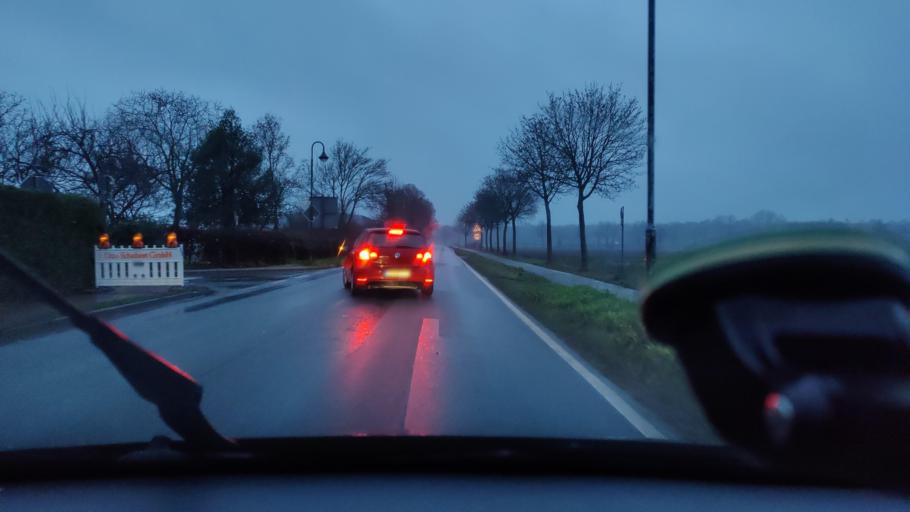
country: DE
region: North Rhine-Westphalia
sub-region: Regierungsbezirk Dusseldorf
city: Sonsbeck
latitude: 51.6004
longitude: 6.3805
